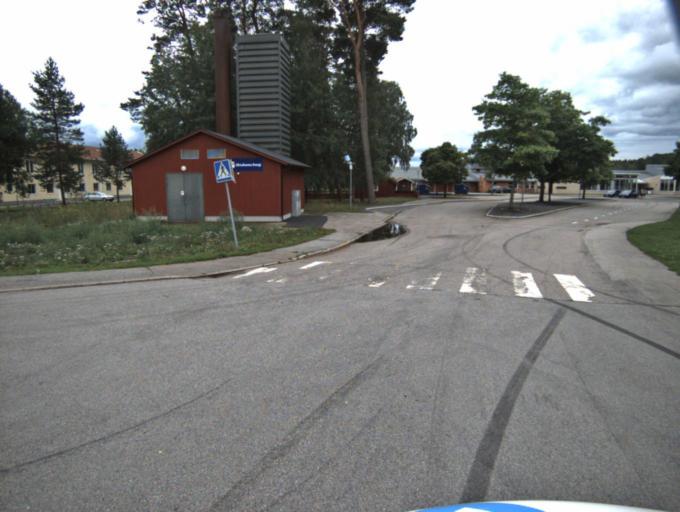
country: SE
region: Vaestra Goetaland
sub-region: Ulricehamns Kommun
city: Ulricehamn
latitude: 57.8580
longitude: 13.4279
